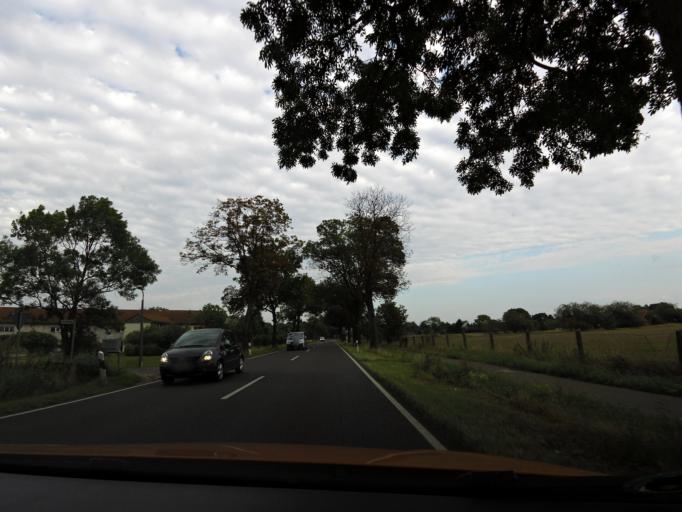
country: DE
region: Brandenburg
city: Gross Kreutz
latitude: 52.4005
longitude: 12.8002
